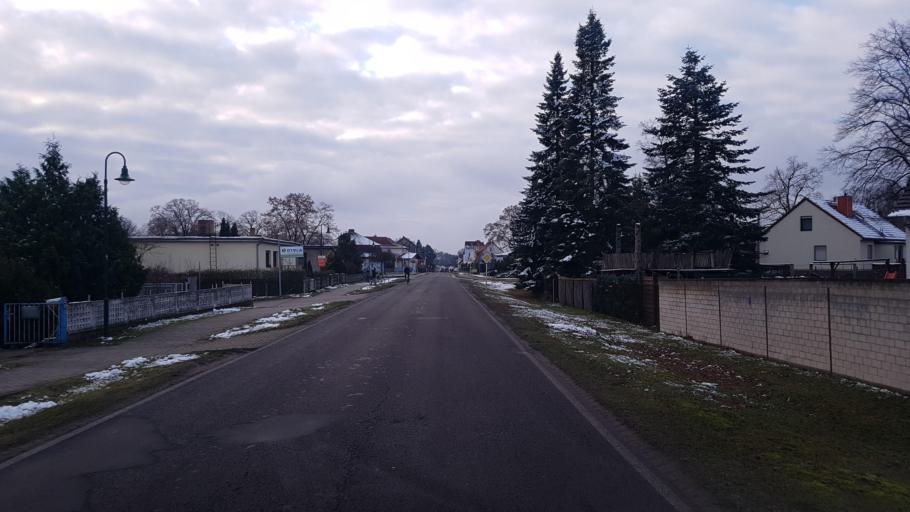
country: DE
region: Brandenburg
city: Rehfelde
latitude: 52.5084
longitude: 13.8574
